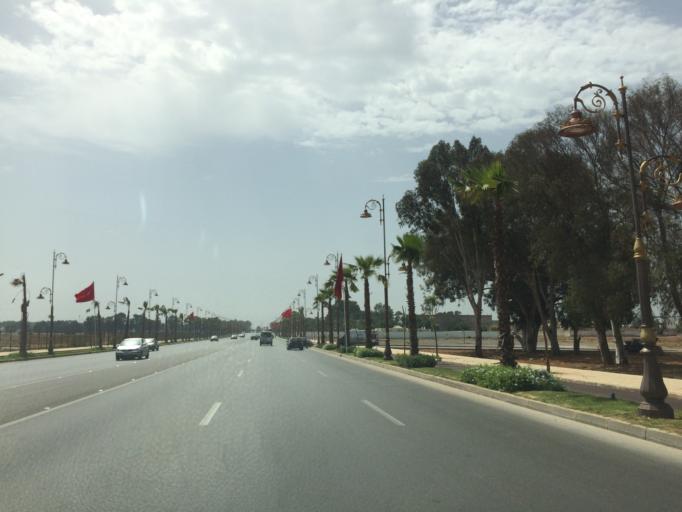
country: MA
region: Rabat-Sale-Zemmour-Zaer
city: Sale
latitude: 34.0324
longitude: -6.7680
